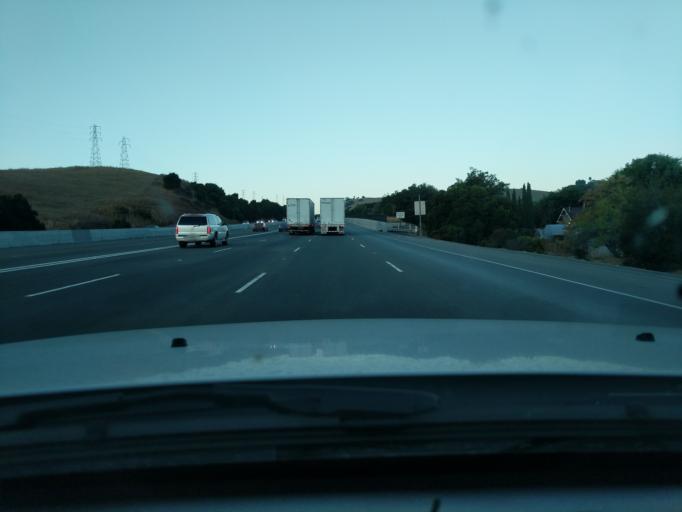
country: US
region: California
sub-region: Alameda County
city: Pleasanton
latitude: 37.5711
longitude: -121.8909
